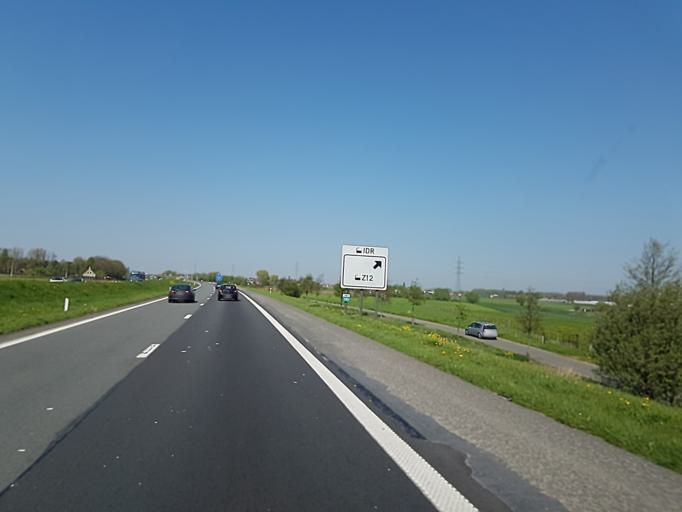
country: BE
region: Flanders
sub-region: Provincie West-Vlaanderen
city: Zonnebeke
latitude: 50.8587
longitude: 2.9679
